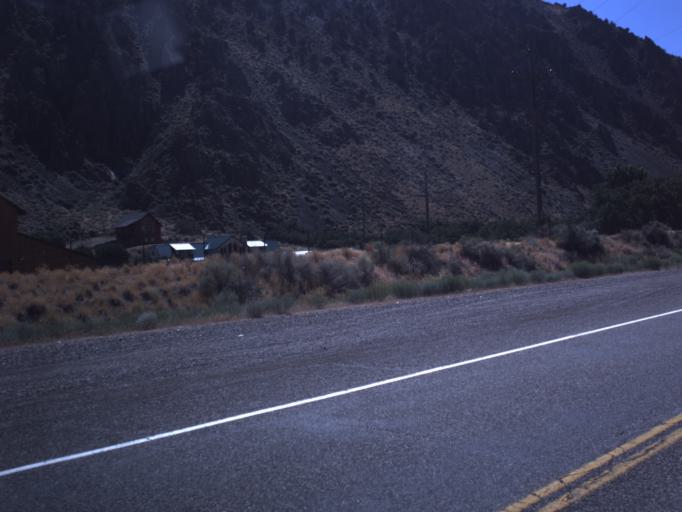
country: US
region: Utah
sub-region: Sevier County
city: Monroe
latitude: 38.5100
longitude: -112.2604
